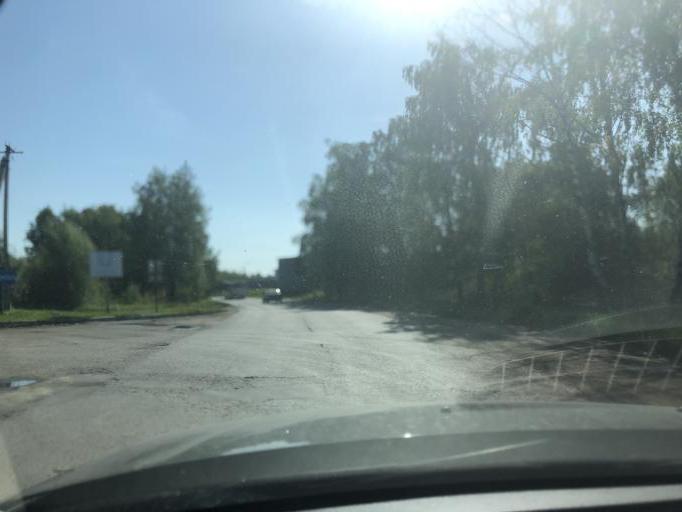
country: RU
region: Tula
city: Skuratovskiy
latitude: 54.1286
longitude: 37.6190
